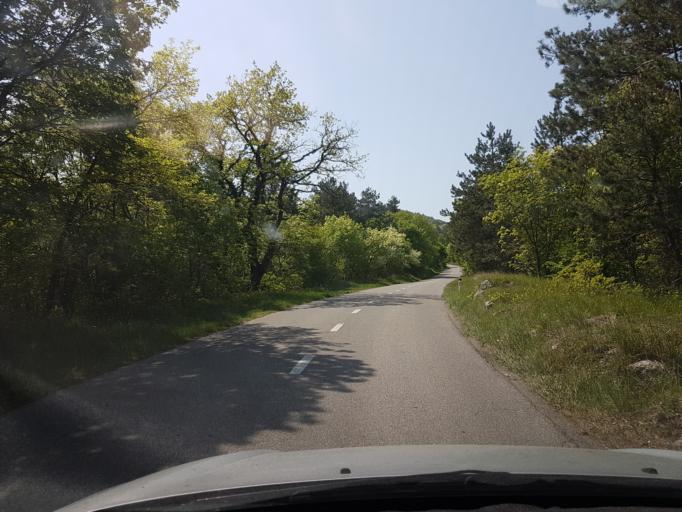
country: IT
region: Friuli Venezia Giulia
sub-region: Provincia di Trieste
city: Aurisina
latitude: 45.7865
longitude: 13.7029
